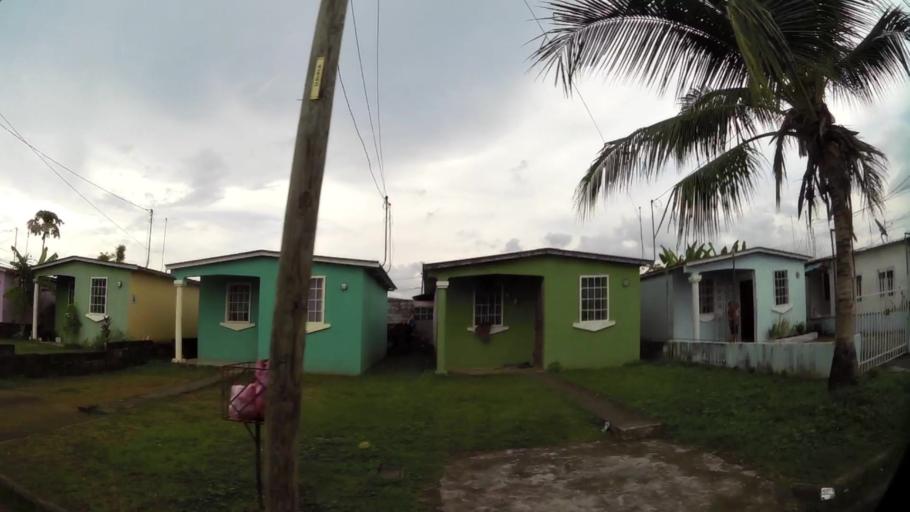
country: PA
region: Panama
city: Cabra Numero Uno
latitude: 9.0853
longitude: -79.3515
